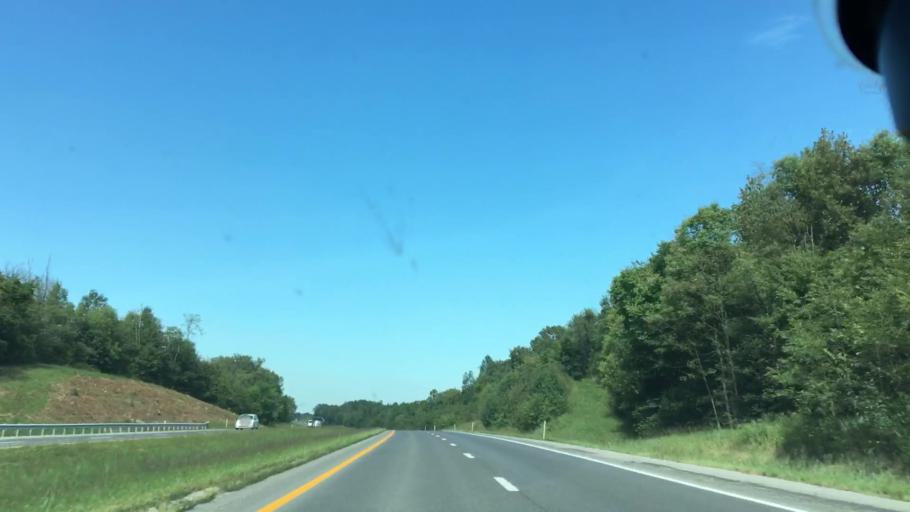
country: US
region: Kentucky
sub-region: Webster County
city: Sebree
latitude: 37.5280
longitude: -87.4756
